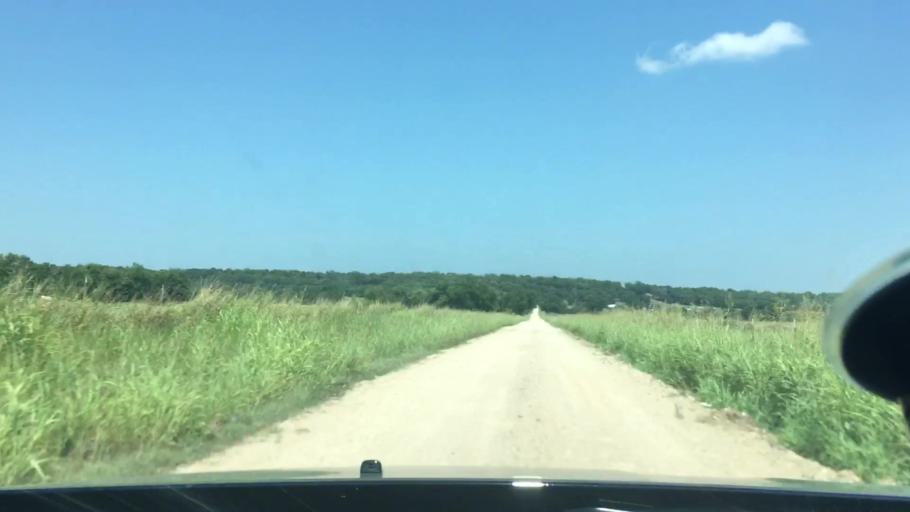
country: US
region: Oklahoma
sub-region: Johnston County
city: Tishomingo
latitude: 34.3535
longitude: -96.4420
